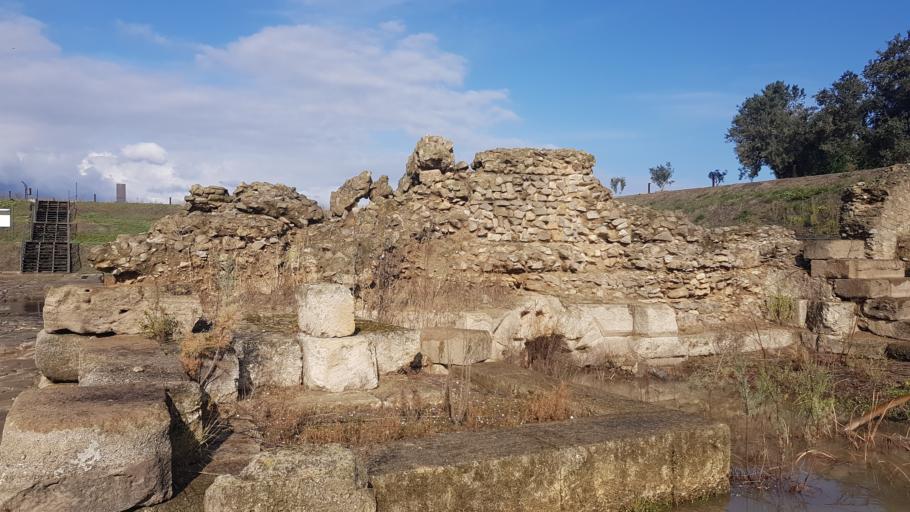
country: IT
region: Calabria
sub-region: Provincia di Cosenza
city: Sibari
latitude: 39.7184
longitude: 16.4889
